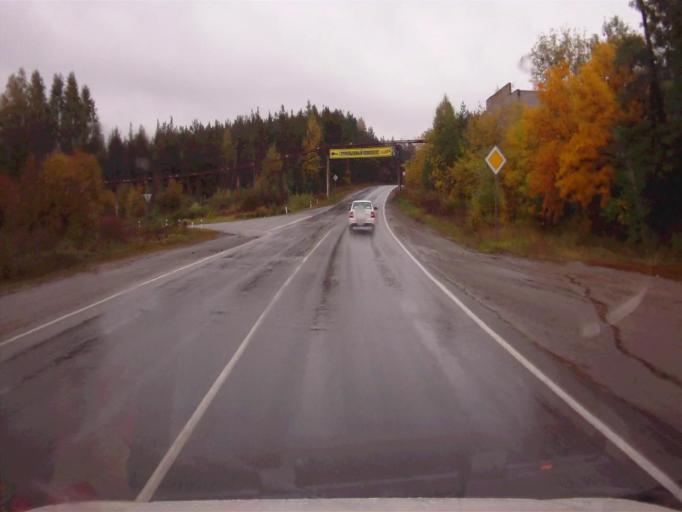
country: RU
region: Chelyabinsk
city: Kyshtym
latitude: 55.7289
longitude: 60.5198
